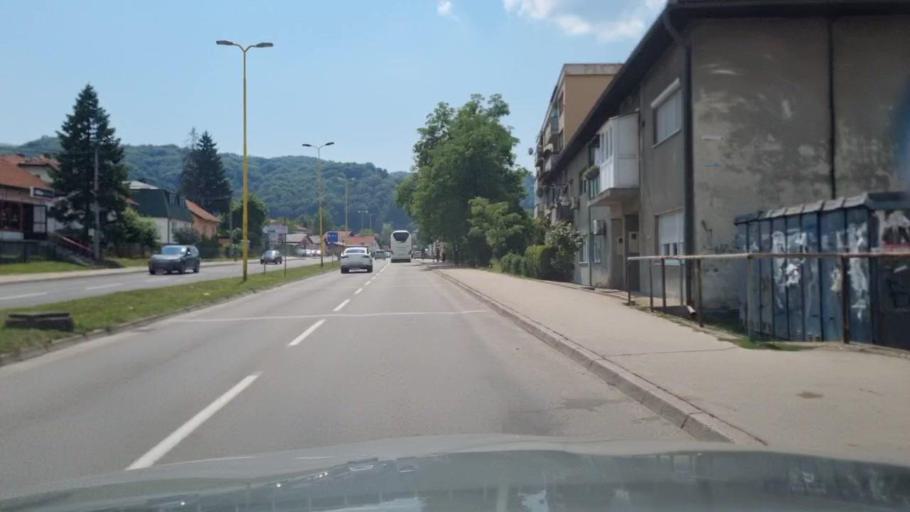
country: BA
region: Federation of Bosnia and Herzegovina
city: Tuzla
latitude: 44.5291
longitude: 18.6430
